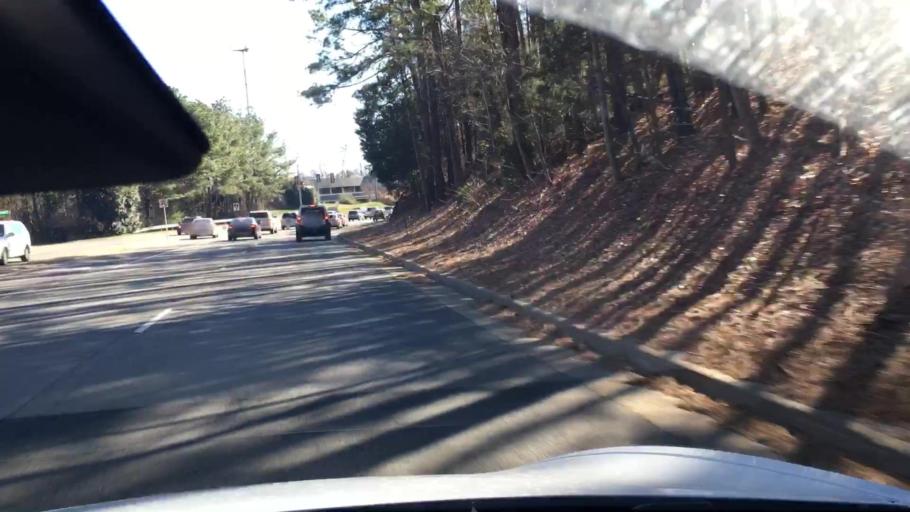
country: US
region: Virginia
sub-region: Henrico County
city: Tuckahoe
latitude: 37.5832
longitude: -77.5695
